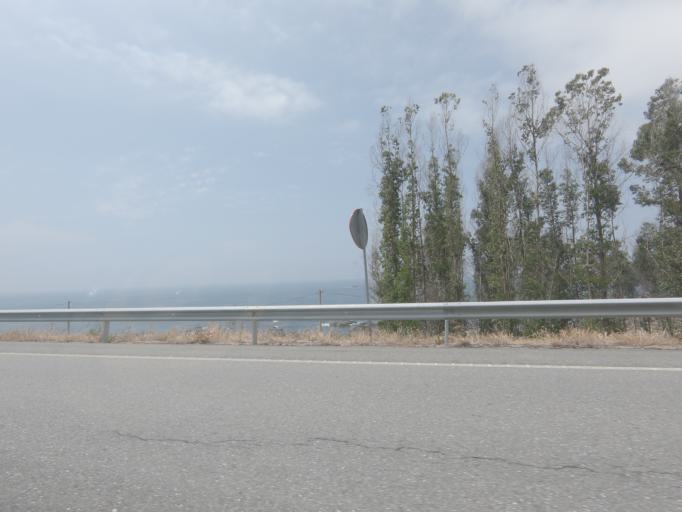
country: ES
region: Galicia
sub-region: Provincia de Pontevedra
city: A Guarda
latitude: 41.9429
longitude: -8.8831
